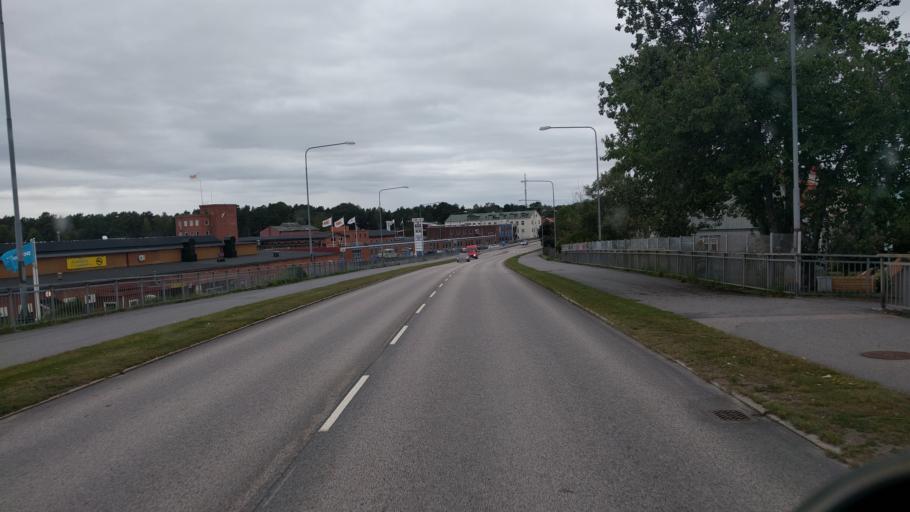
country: SE
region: Kalmar
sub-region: Vasterviks Kommun
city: Vaestervik
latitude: 57.7525
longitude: 16.6277
